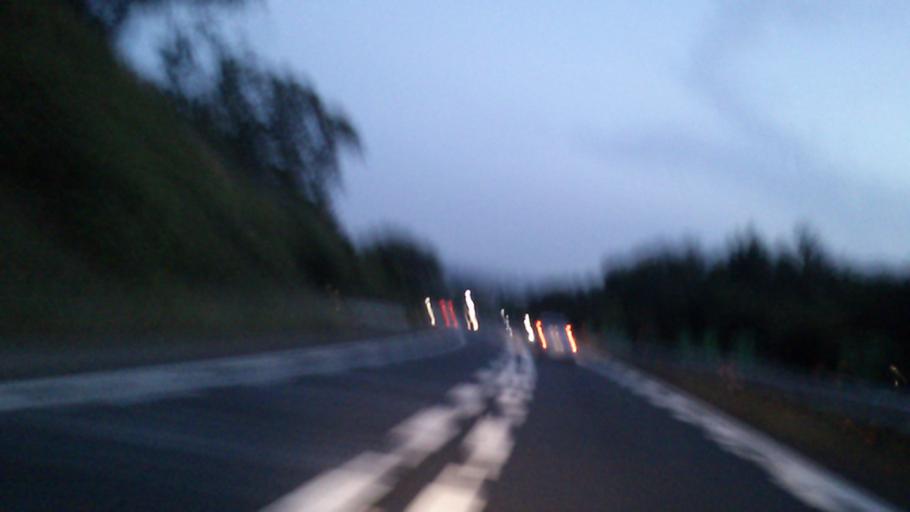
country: JP
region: Aichi
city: Kasugai
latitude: 35.3208
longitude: 137.0198
